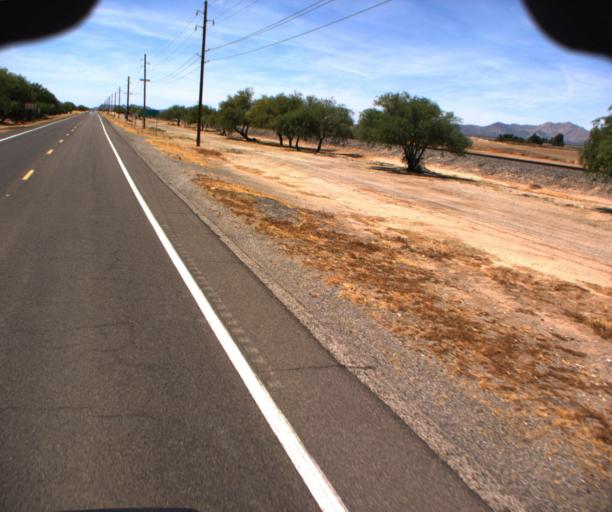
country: US
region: Arizona
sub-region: La Paz County
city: Salome
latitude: 33.8192
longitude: -113.5472
